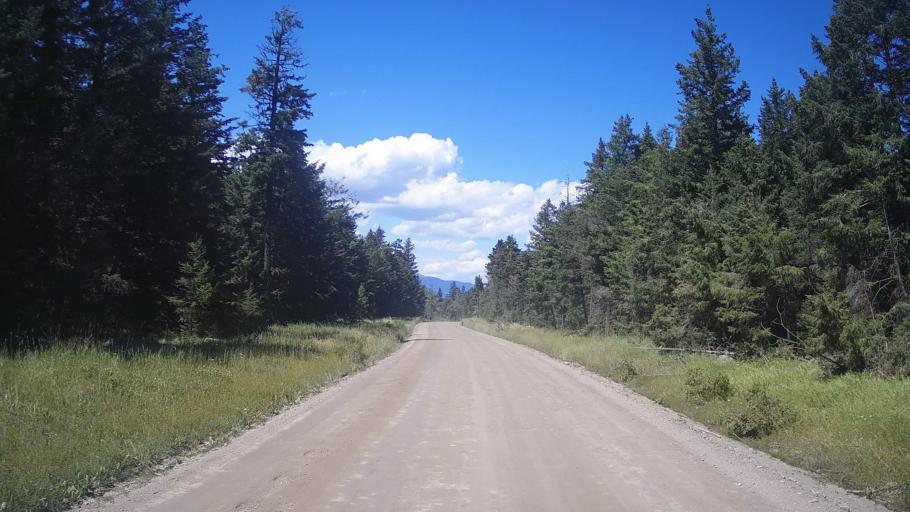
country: CA
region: British Columbia
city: Cache Creek
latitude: 51.1522
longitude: -121.5368
